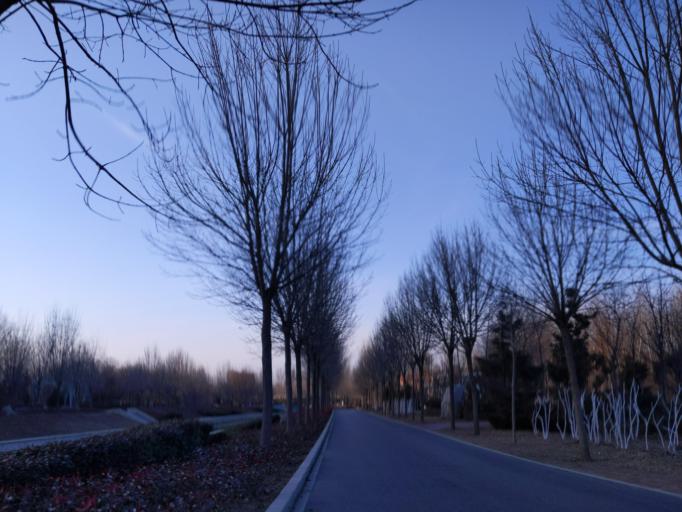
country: CN
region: Henan Sheng
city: Puyang
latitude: 35.7682
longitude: 114.9995
